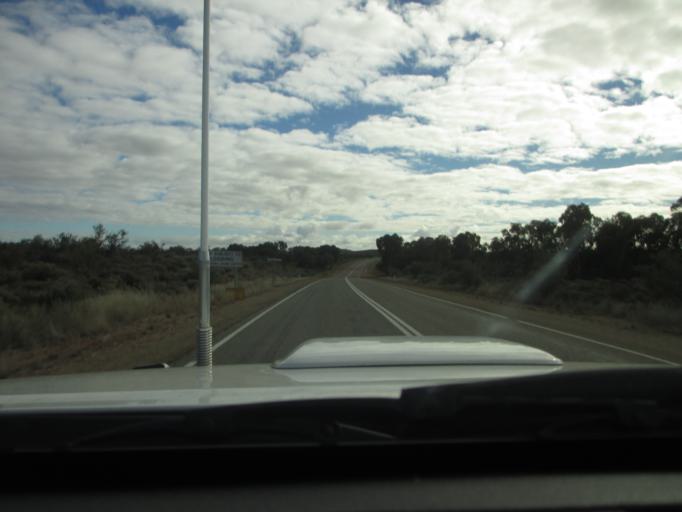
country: AU
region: South Australia
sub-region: Flinders Ranges
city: Quorn
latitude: -32.3763
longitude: 138.4997
